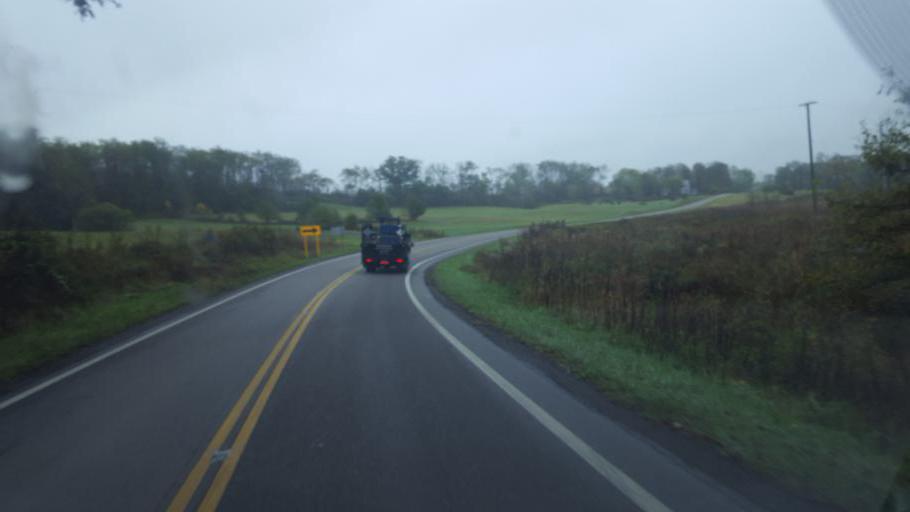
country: US
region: Ohio
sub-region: Tuscarawas County
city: Rockford
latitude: 40.4253
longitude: -81.1586
